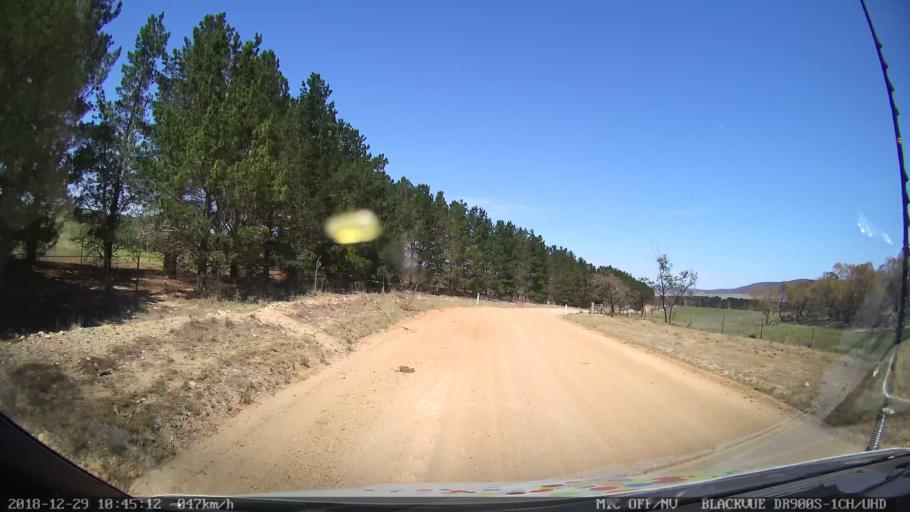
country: AU
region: New South Wales
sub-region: Palerang
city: Bungendore
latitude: -35.0456
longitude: 149.5229
